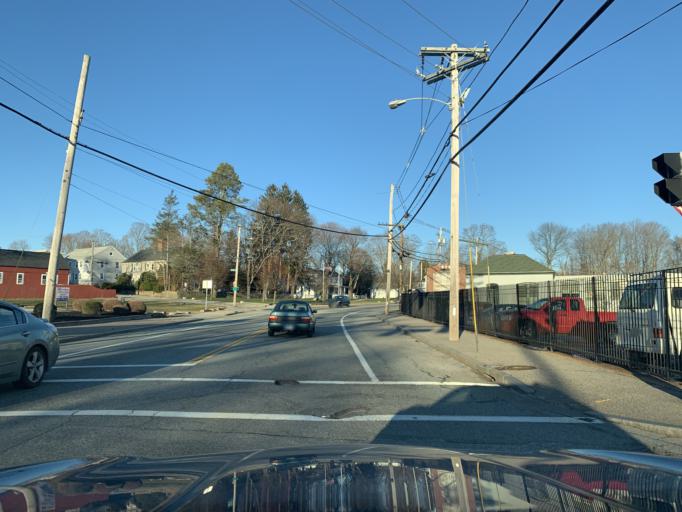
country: US
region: Rhode Island
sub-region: Kent County
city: West Warwick
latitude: 41.6963
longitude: -71.5475
